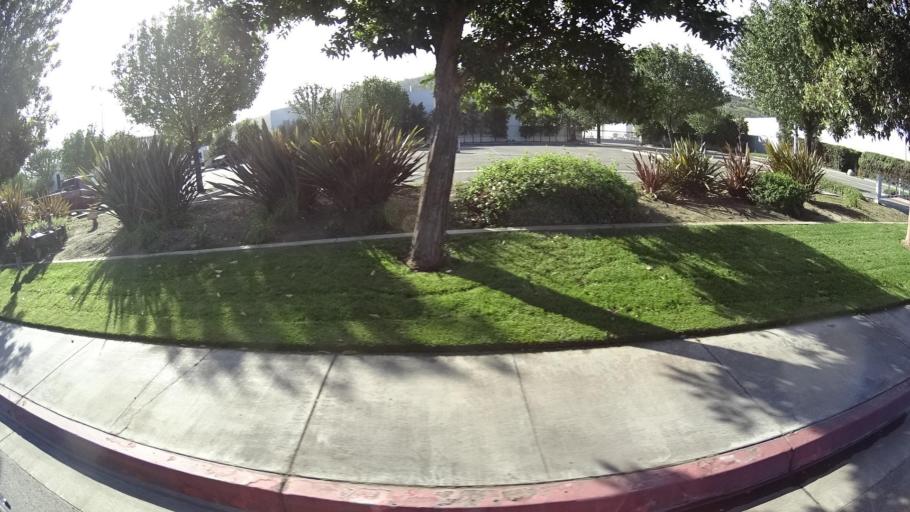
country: US
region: California
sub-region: Los Angeles County
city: South El Monte
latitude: 34.0315
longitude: -118.0293
